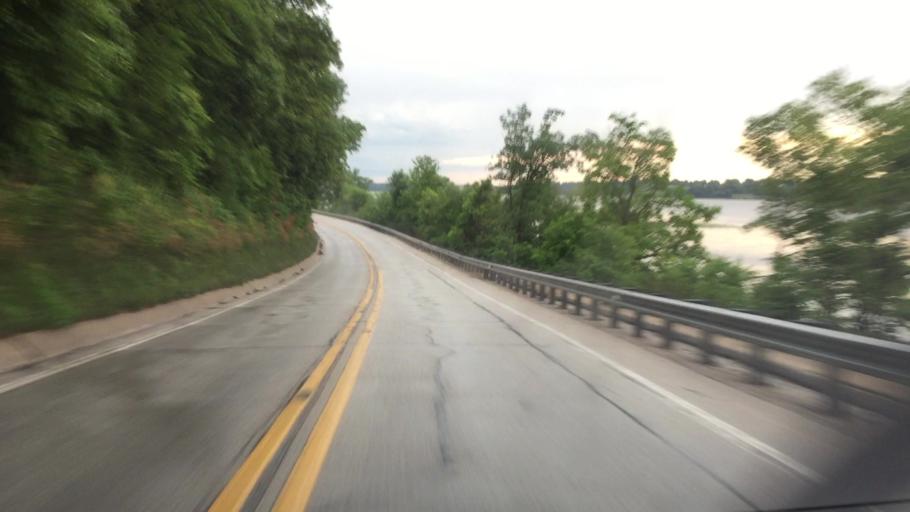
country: US
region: Iowa
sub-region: Lee County
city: Keokuk
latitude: 40.4389
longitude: -91.3717
